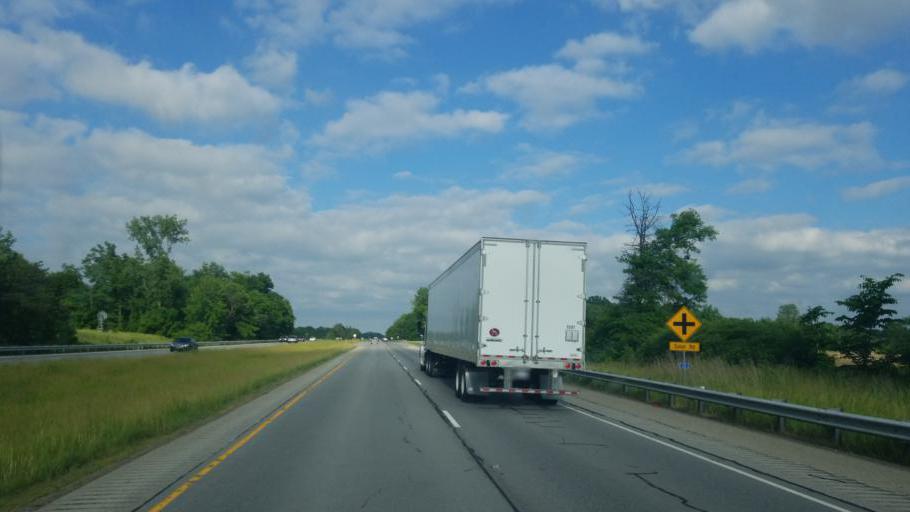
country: US
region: Indiana
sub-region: Whitley County
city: Churubusco
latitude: 41.1258
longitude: -85.3031
